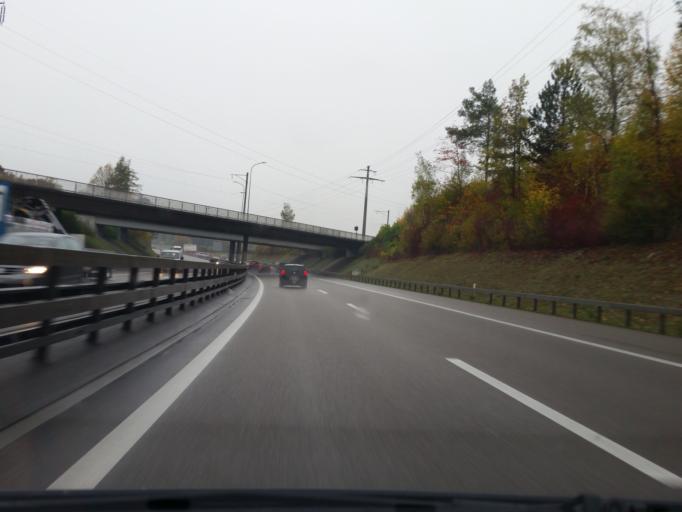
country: CH
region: Zurich
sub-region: Bezirk Winterthur
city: Oberwinterthur (Kreis 2) / Zinzikon
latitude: 47.5302
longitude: 8.7525
